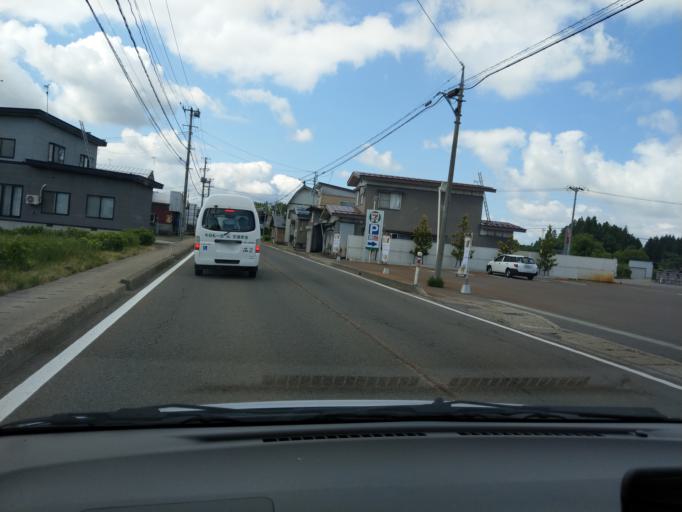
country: JP
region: Akita
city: Yokotemachi
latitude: 39.2823
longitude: 140.5590
